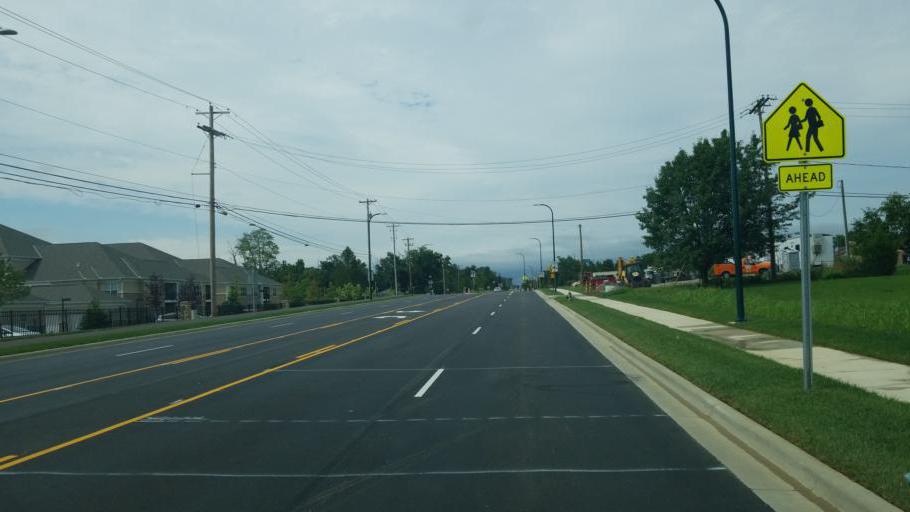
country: US
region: Ohio
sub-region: Franklin County
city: Gahanna
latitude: 40.0299
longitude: -82.8656
